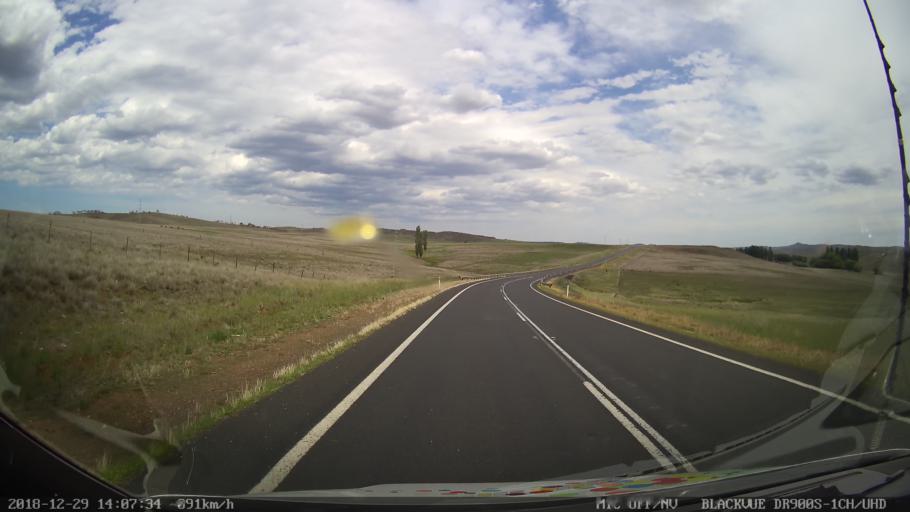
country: AU
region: New South Wales
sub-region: Cooma-Monaro
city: Cooma
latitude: -36.3534
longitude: 149.2145
